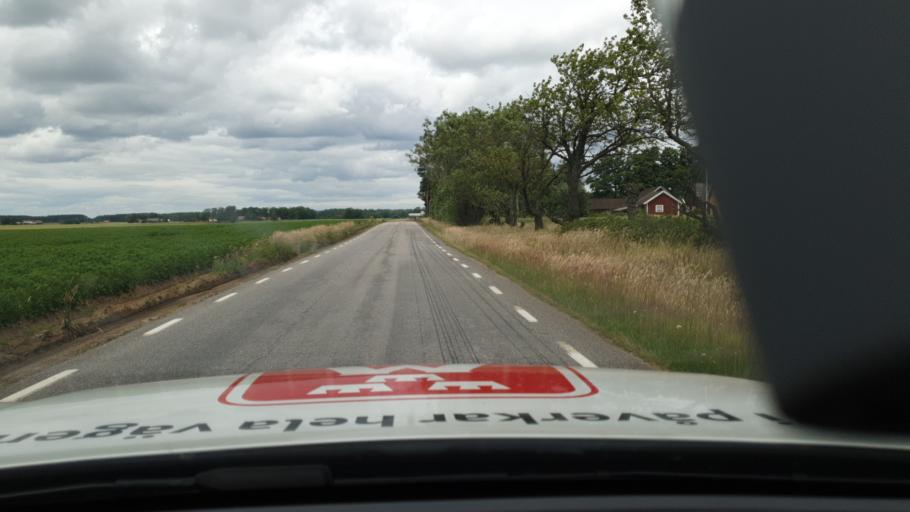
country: SE
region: Vaestra Goetaland
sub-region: Lidkopings Kommun
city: Vinninga
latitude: 58.3793
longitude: 13.3134
